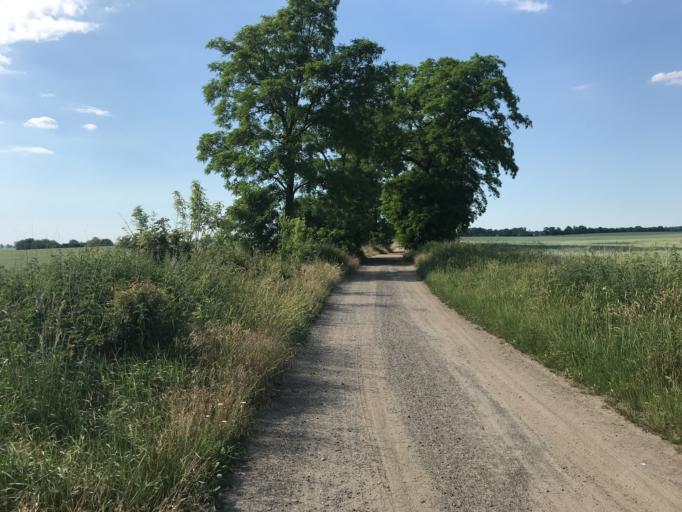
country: PL
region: West Pomeranian Voivodeship
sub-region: Powiat mysliborski
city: Boleszkowice
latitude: 52.7455
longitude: 14.5537
